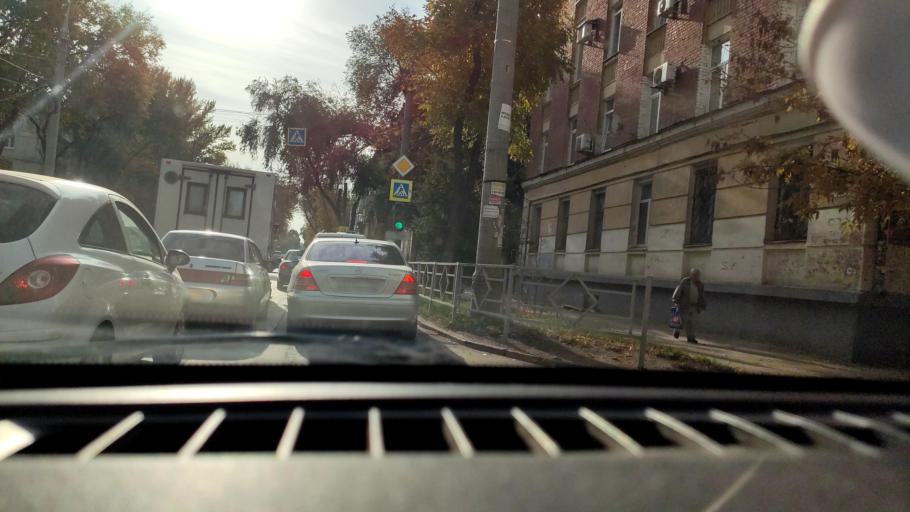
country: RU
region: Samara
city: Samara
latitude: 53.2096
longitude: 50.2462
